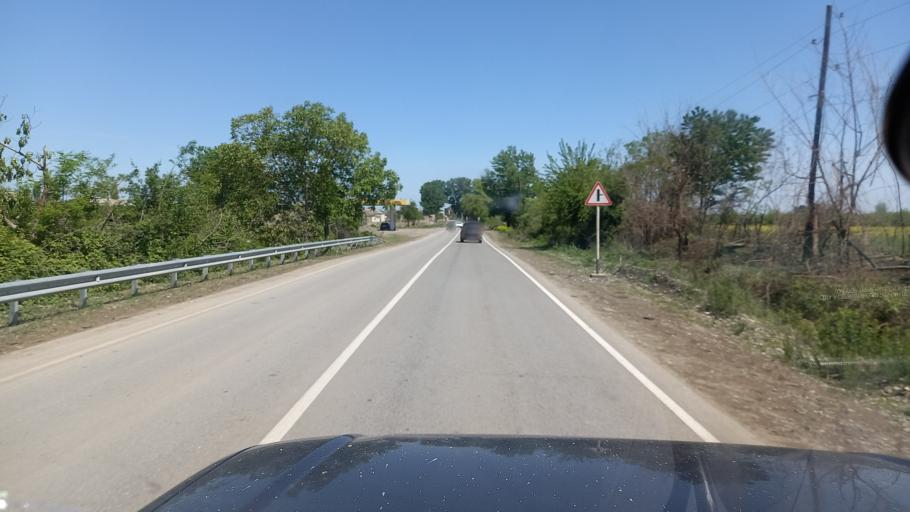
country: RU
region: Dagestan
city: Samur
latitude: 41.7787
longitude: 48.4990
